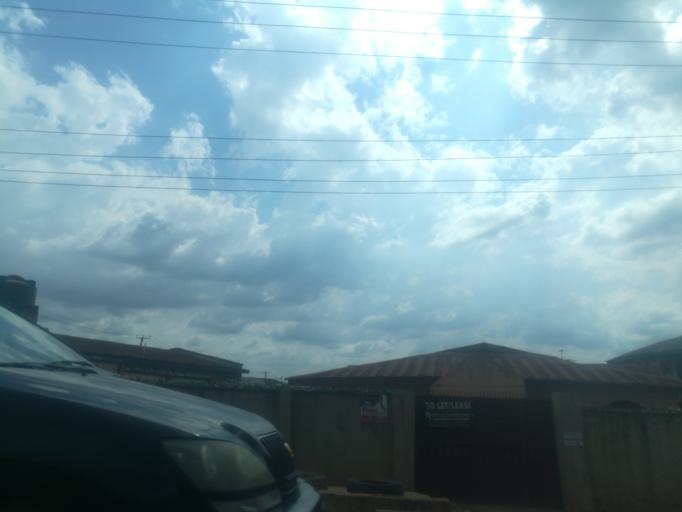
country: NG
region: Oyo
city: Ibadan
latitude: 7.4281
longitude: 3.8390
